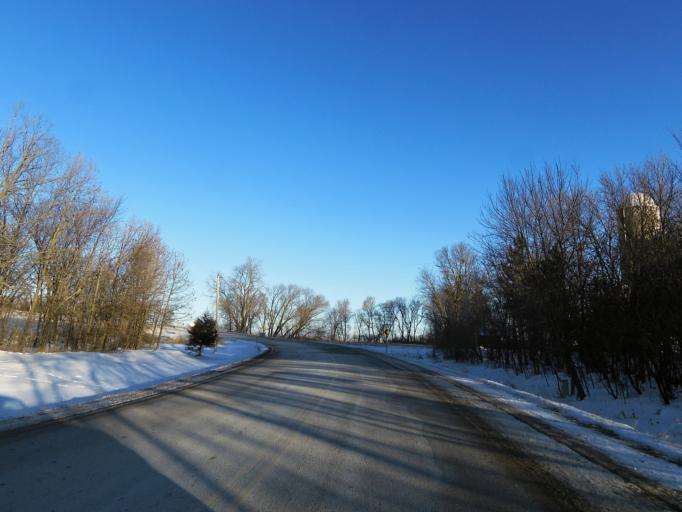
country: US
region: Minnesota
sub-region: Scott County
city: Jordan
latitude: 44.6619
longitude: -93.5317
